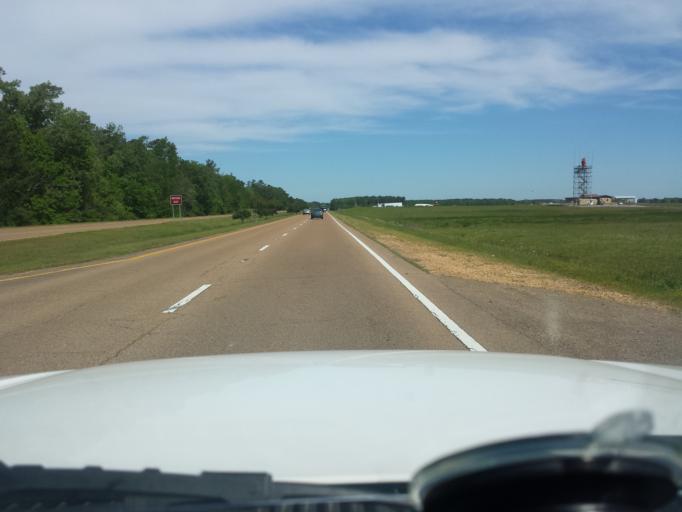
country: US
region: Mississippi
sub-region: Rankin County
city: Pearl
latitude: 32.3021
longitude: -90.0835
